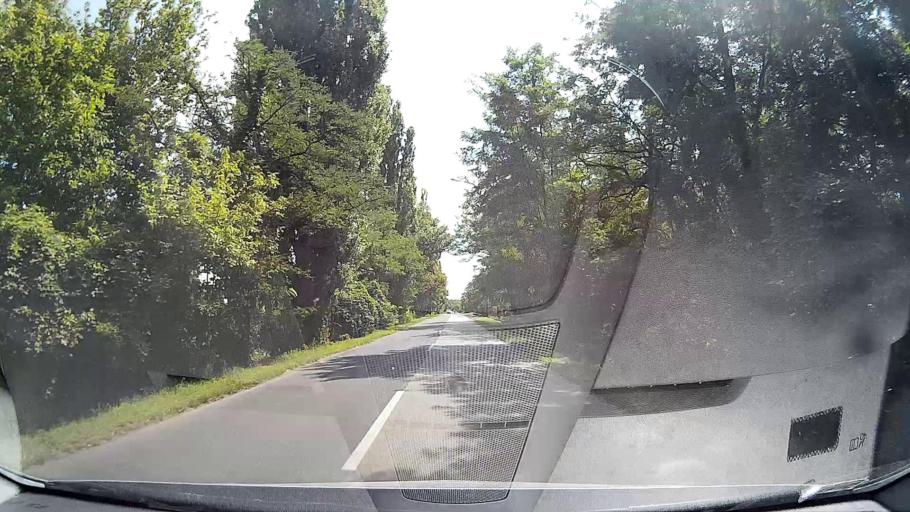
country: HU
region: Pest
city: Tahitotfalu
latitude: 47.7405
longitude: 19.1001
